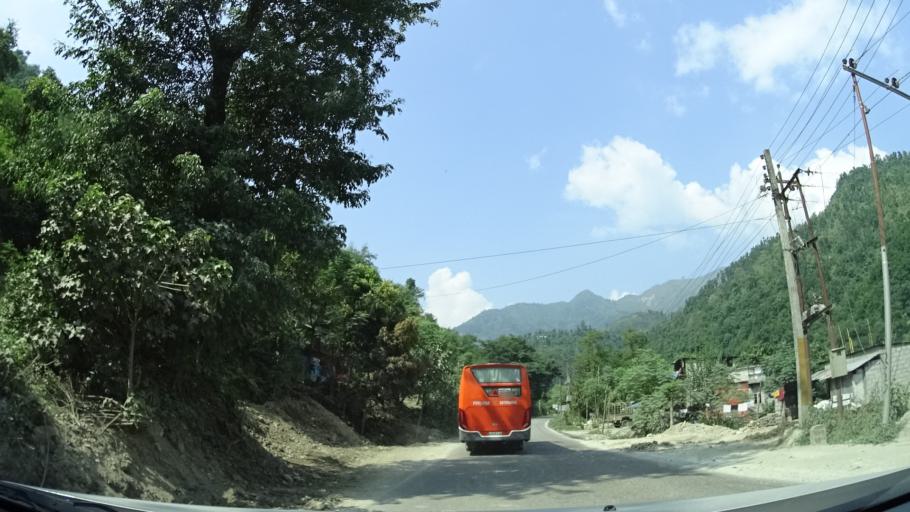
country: NP
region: Central Region
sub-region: Narayani Zone
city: Bharatpur
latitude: 27.8445
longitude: 84.6605
